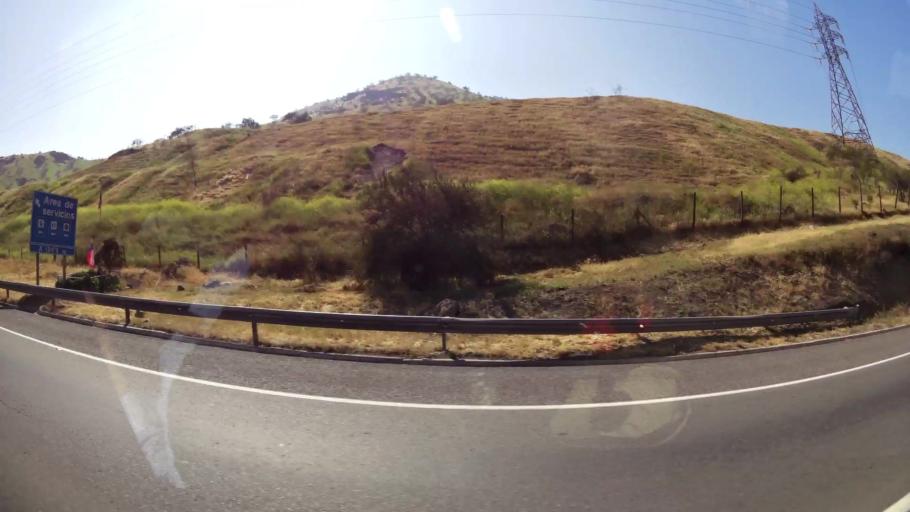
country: CL
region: Santiago Metropolitan
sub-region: Provincia de Chacabuco
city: Chicureo Abajo
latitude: -33.3231
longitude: -70.7055
